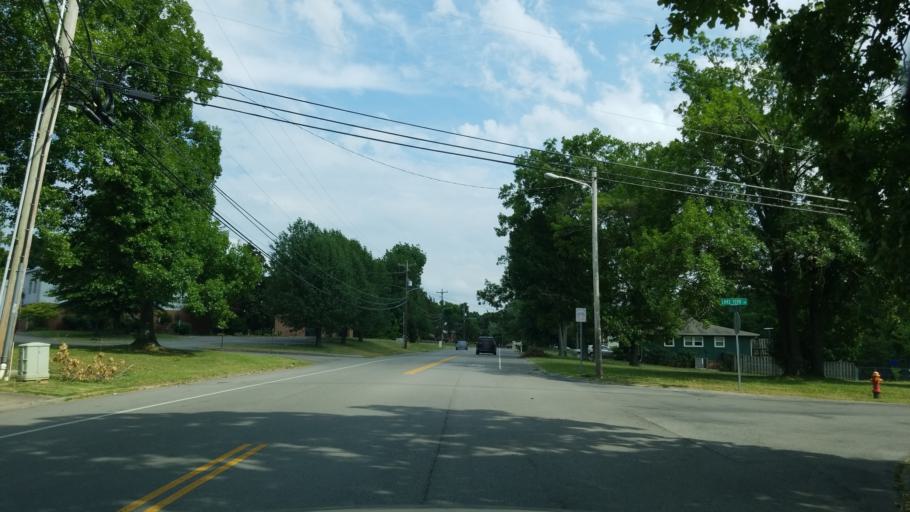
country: US
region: Tennessee
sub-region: Rutherford County
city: La Vergne
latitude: 36.0881
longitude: -86.6148
